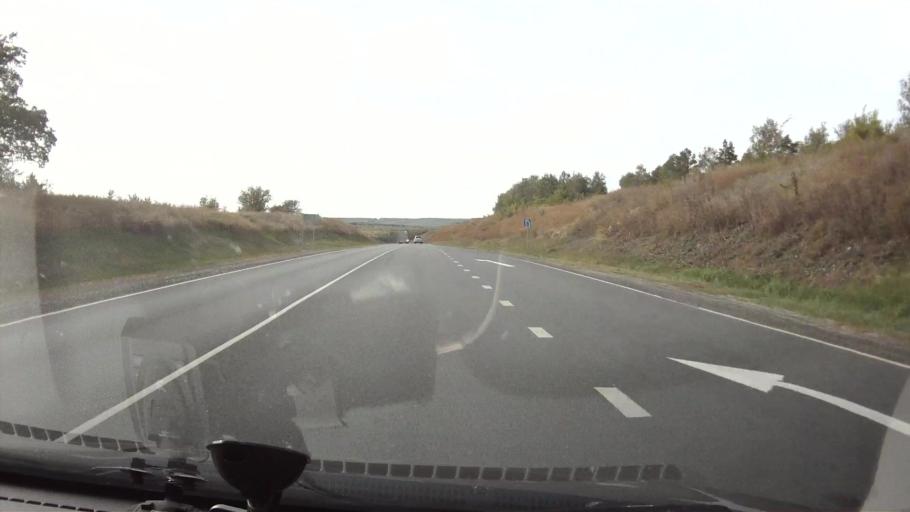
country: RU
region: Saratov
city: Tersa
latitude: 52.1028
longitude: 47.5012
